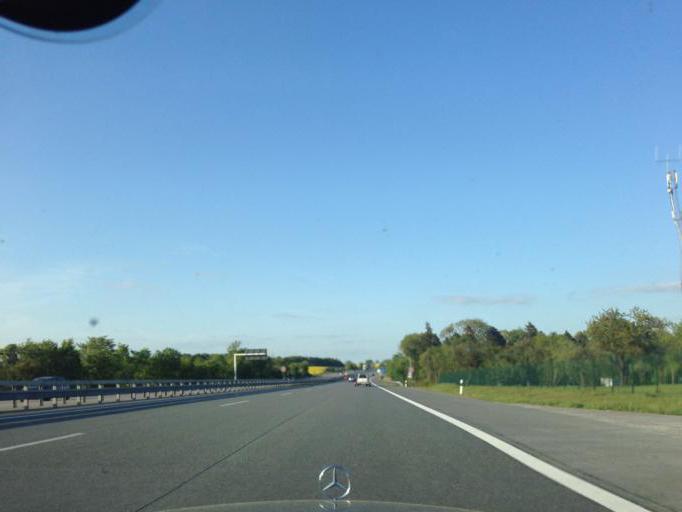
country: DE
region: Schleswig-Holstein
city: Politz
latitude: 53.7863
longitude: 10.4202
